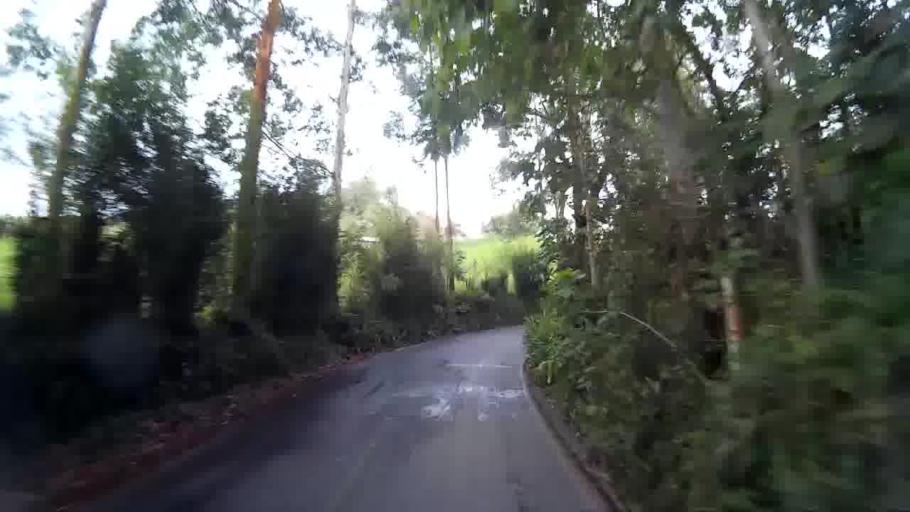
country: CO
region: Quindio
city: Filandia
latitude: 4.6833
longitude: -75.6574
